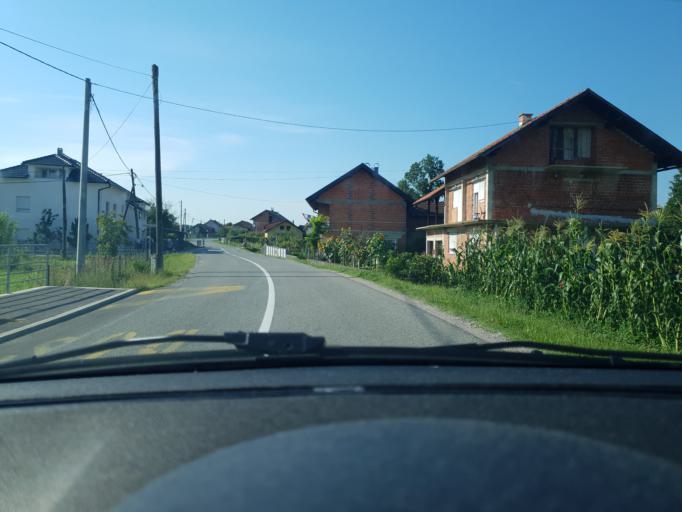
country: HR
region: Zagrebacka
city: Jakovlje
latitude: 45.9323
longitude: 15.8451
